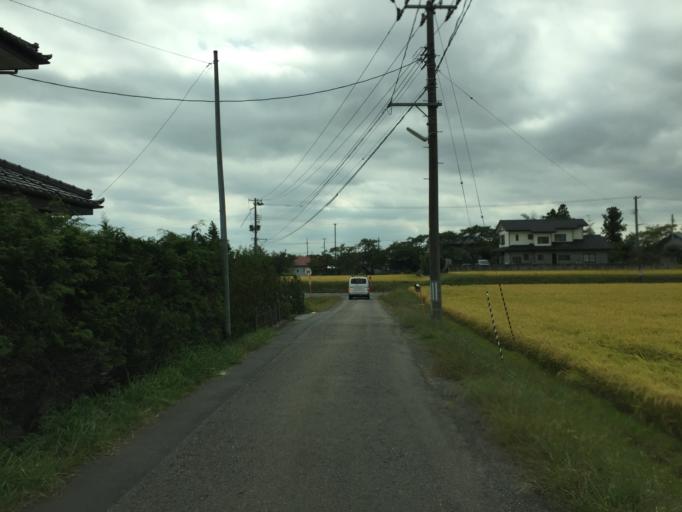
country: JP
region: Fukushima
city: Koriyama
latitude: 37.4610
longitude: 140.3513
